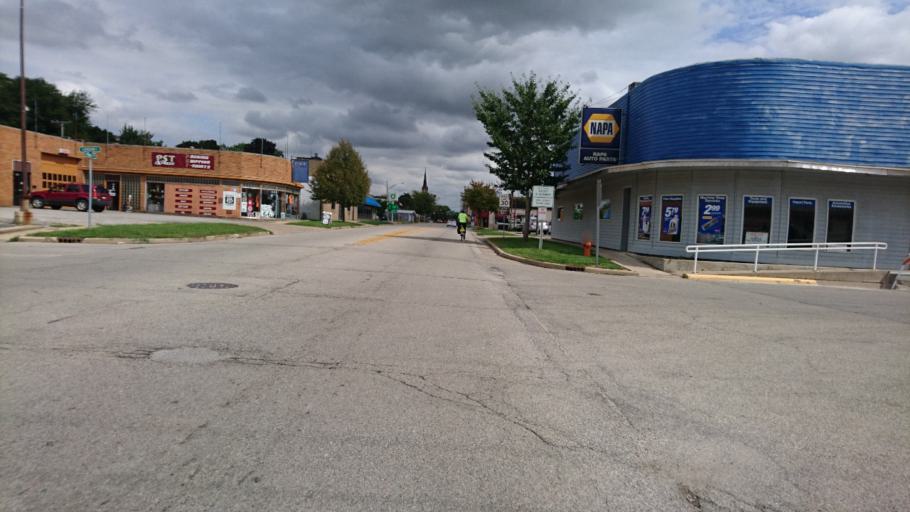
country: US
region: Illinois
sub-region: Livingston County
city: Pontiac
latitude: 40.8810
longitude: -88.6334
